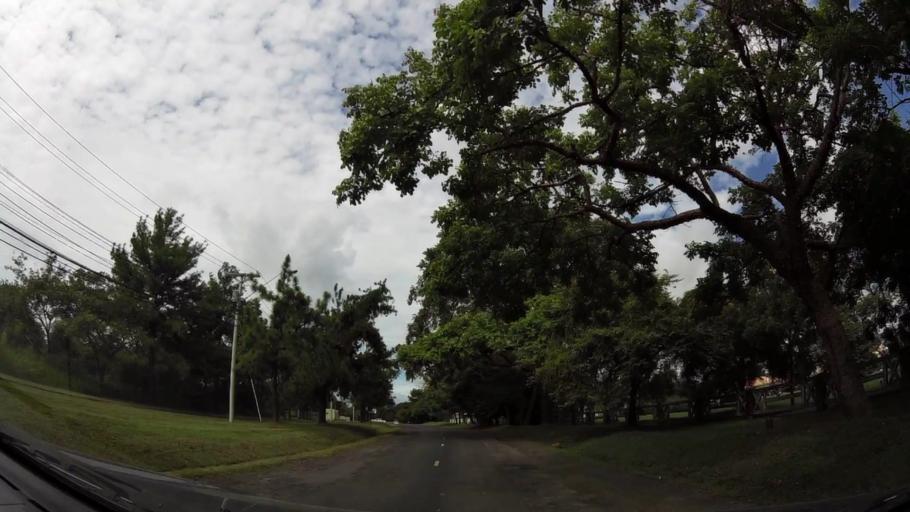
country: PA
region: Panama
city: Nueva Gorgona
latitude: 8.5364
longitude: -79.8997
